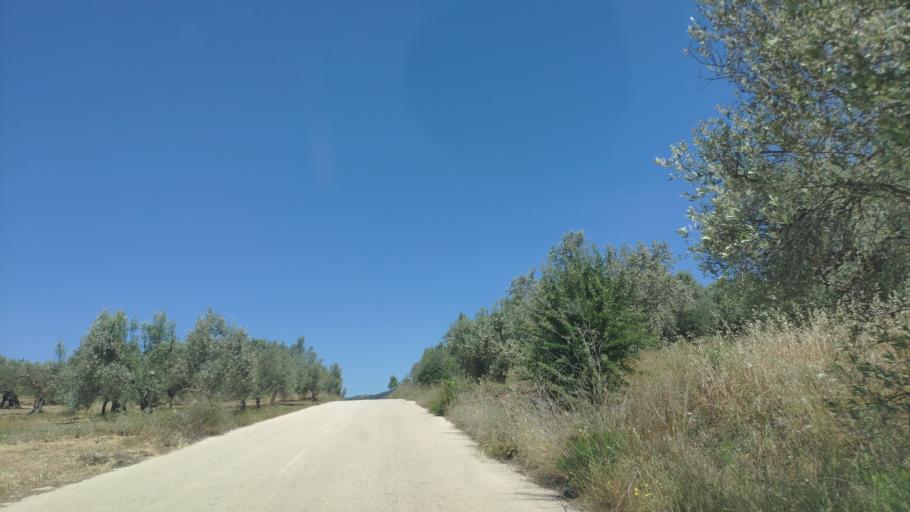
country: GR
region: Peloponnese
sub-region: Nomos Korinthias
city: Athikia
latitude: 37.8309
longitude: 22.9282
